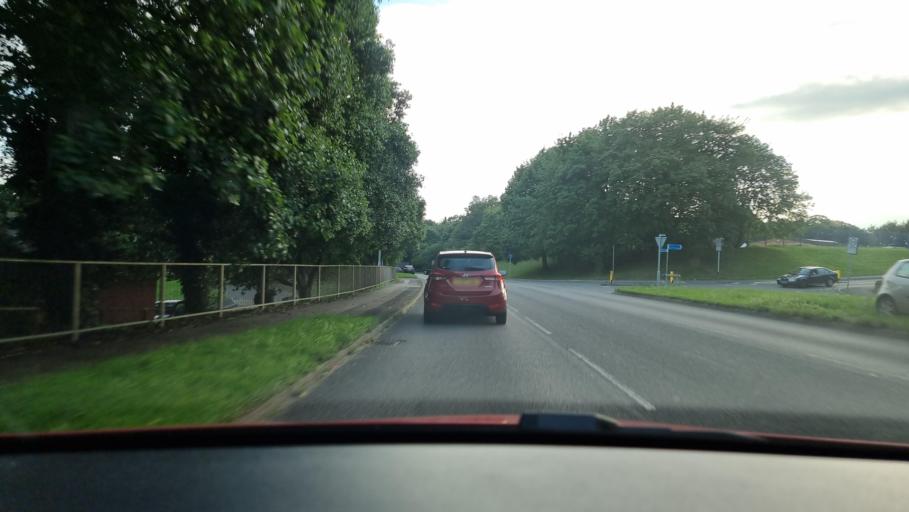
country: GB
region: England
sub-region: Northamptonshire
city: Northampton
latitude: 52.2523
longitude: -0.9211
